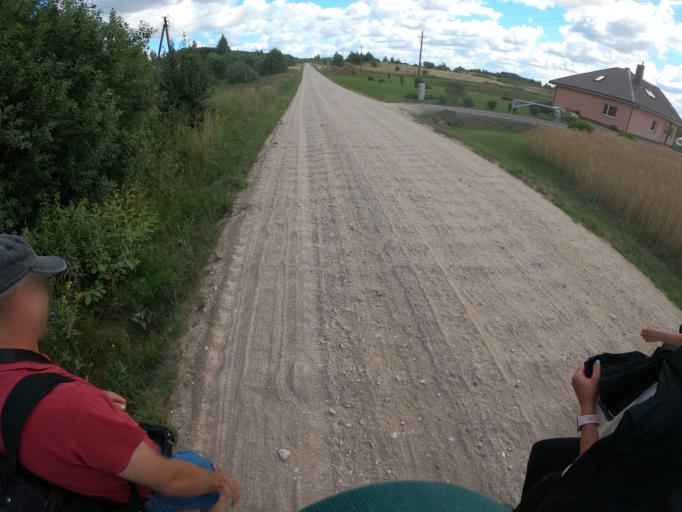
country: LT
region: Alytaus apskritis
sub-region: Alytus
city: Alytus
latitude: 54.3319
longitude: 24.0790
